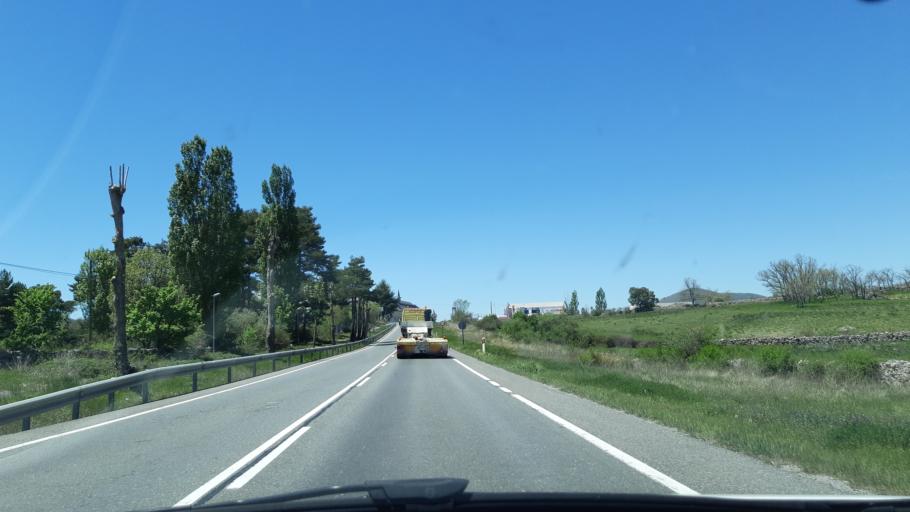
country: ES
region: Castille and Leon
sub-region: Provincia de Avila
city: Peguerinos
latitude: 40.7168
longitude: -4.2036
